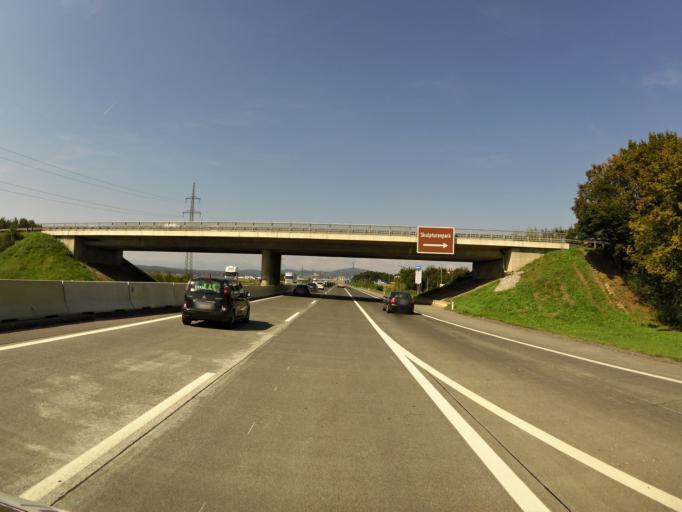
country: AT
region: Styria
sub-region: Politischer Bezirk Graz-Umgebung
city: Zettling
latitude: 46.9623
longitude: 15.4379
